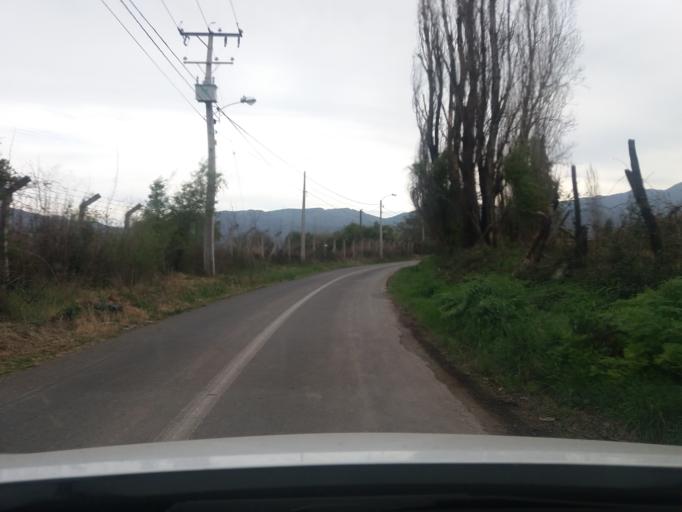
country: CL
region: Valparaiso
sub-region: Provincia de Los Andes
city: Los Andes
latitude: -32.8577
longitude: -70.6469
